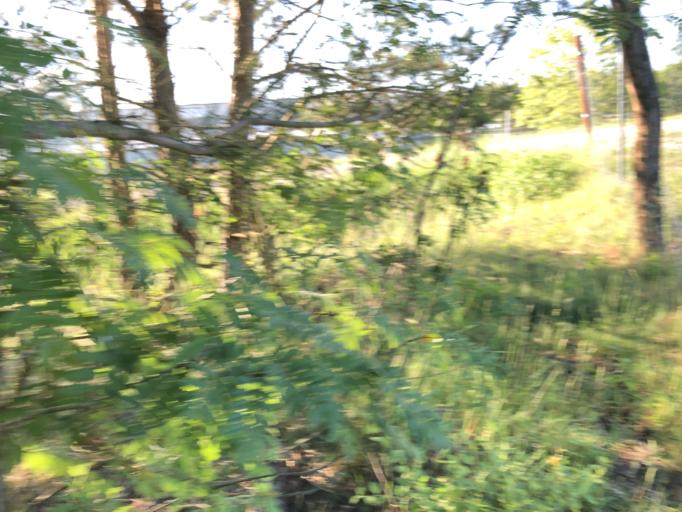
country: DE
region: Bavaria
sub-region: Upper Franconia
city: Memmelsdorf
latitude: 49.9141
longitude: 10.9461
